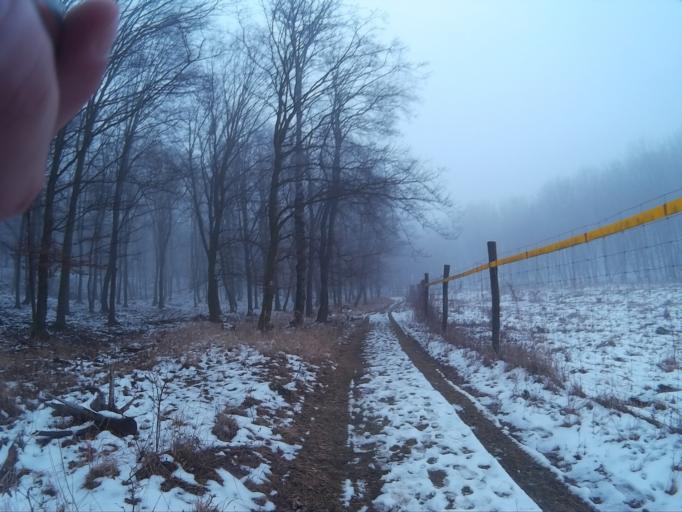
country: HU
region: Komarom-Esztergom
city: Tardos
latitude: 47.6642
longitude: 18.4753
